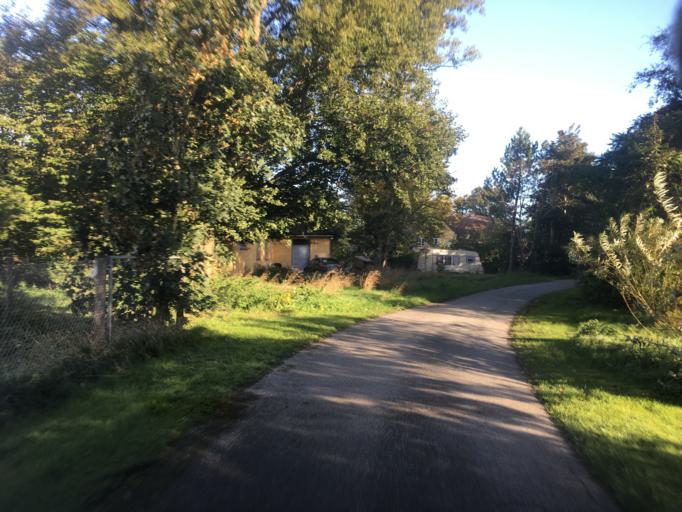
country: DE
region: Schleswig-Holstein
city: Ellhoft
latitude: 54.9625
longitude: 9.0113
